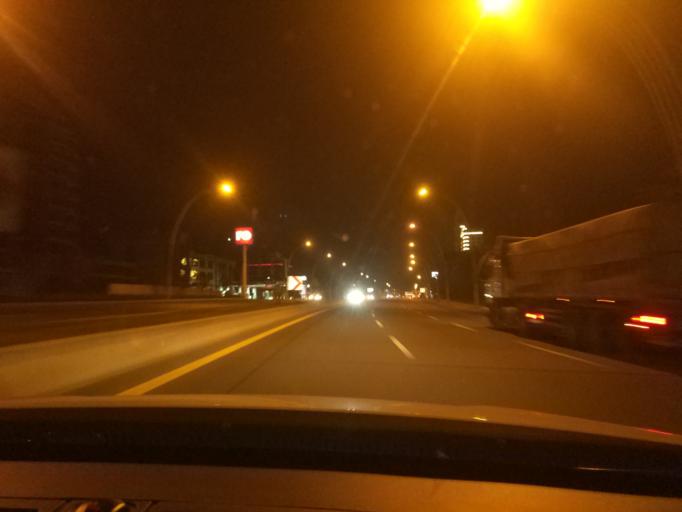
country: TR
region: Ankara
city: Mamak
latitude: 40.0670
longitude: 32.9245
